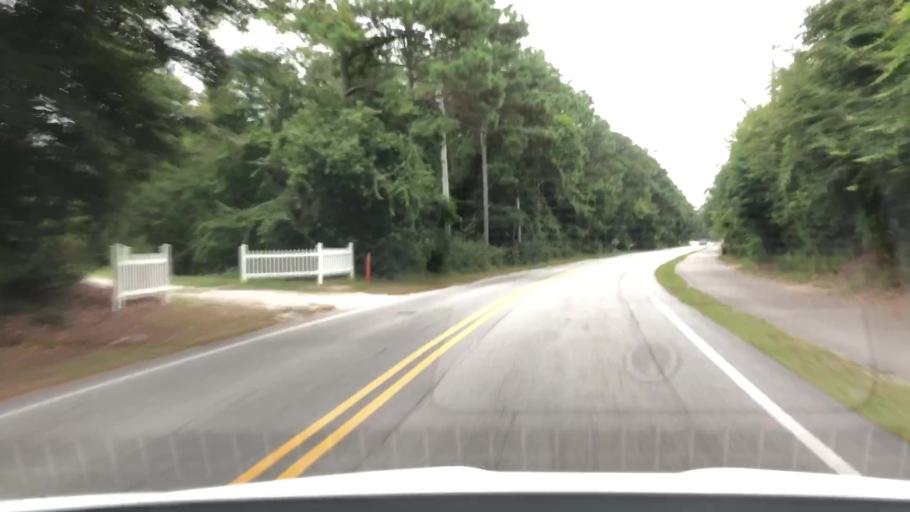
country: US
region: North Carolina
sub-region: Carteret County
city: Cedar Point
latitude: 34.6591
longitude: -77.0667
